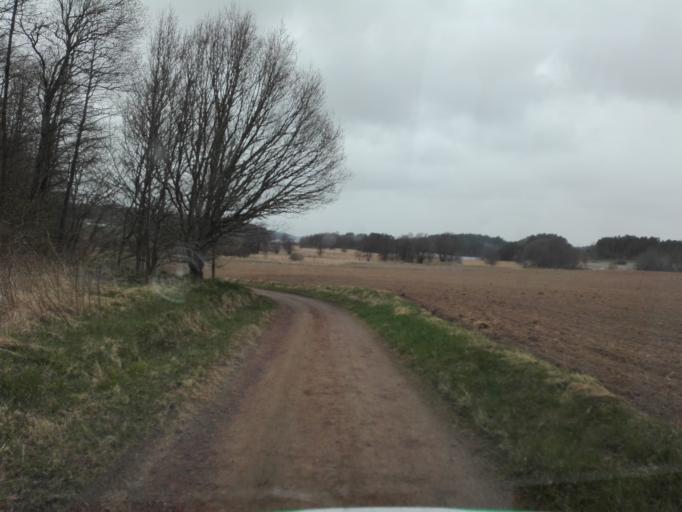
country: SE
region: OEstergoetland
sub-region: Linkopings Kommun
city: Sturefors
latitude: 58.2948
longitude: 15.8624
